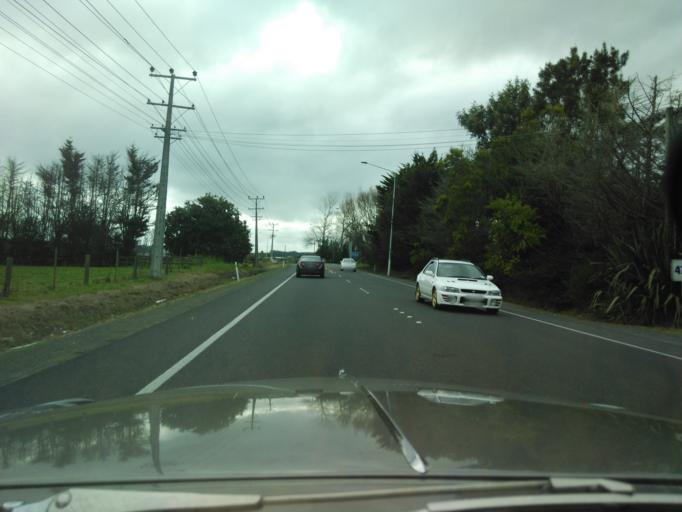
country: NZ
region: Auckland
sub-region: Auckland
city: Muriwai Beach
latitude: -36.7823
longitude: 174.5707
